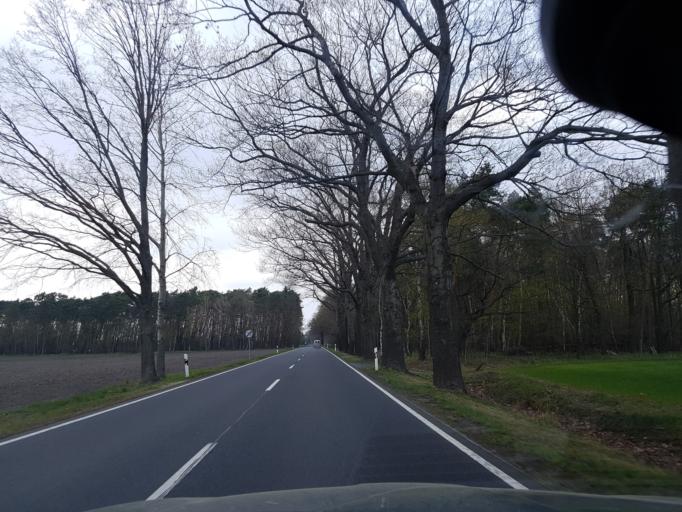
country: DE
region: Brandenburg
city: Schraden
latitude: 51.4333
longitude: 13.7061
